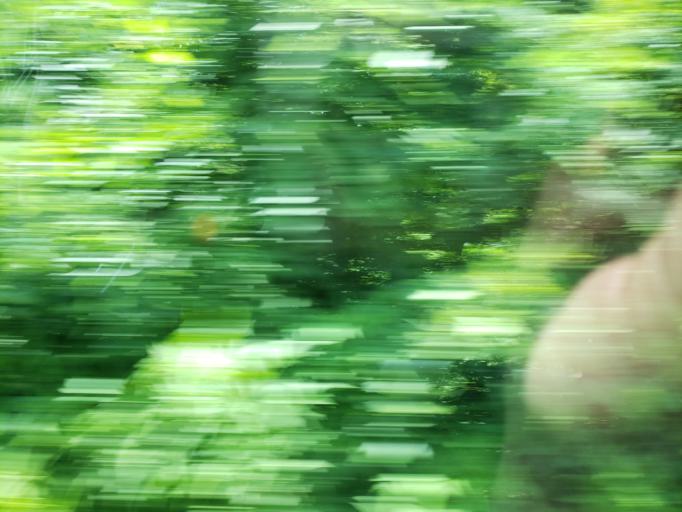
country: ID
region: Bali
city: Kangin
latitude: -8.8371
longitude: 115.1367
